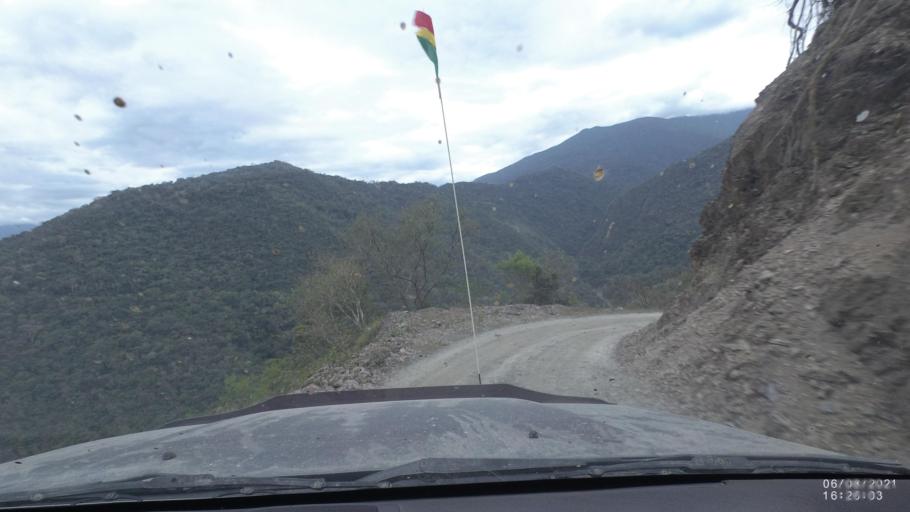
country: BO
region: La Paz
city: Quime
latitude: -16.5336
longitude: -66.7581
